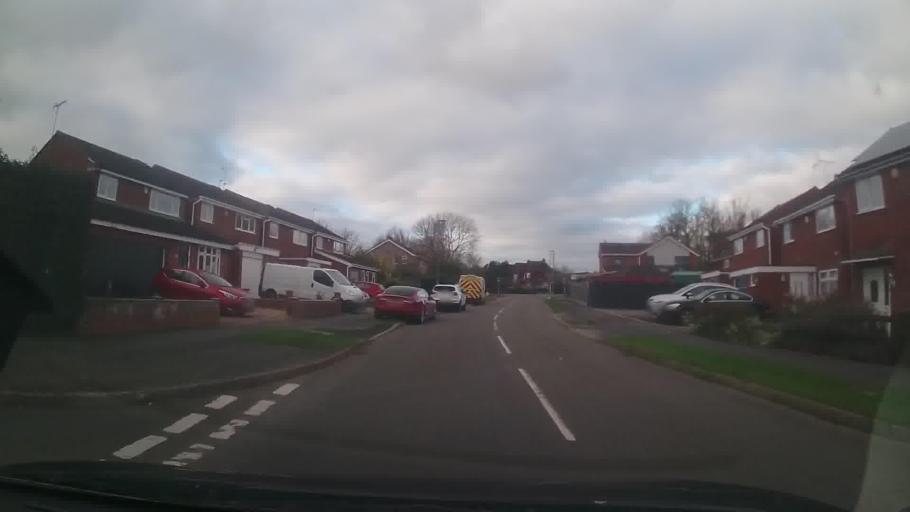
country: GB
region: England
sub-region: Leicestershire
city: Kirby Muxloe
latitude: 52.6502
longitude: -1.2415
